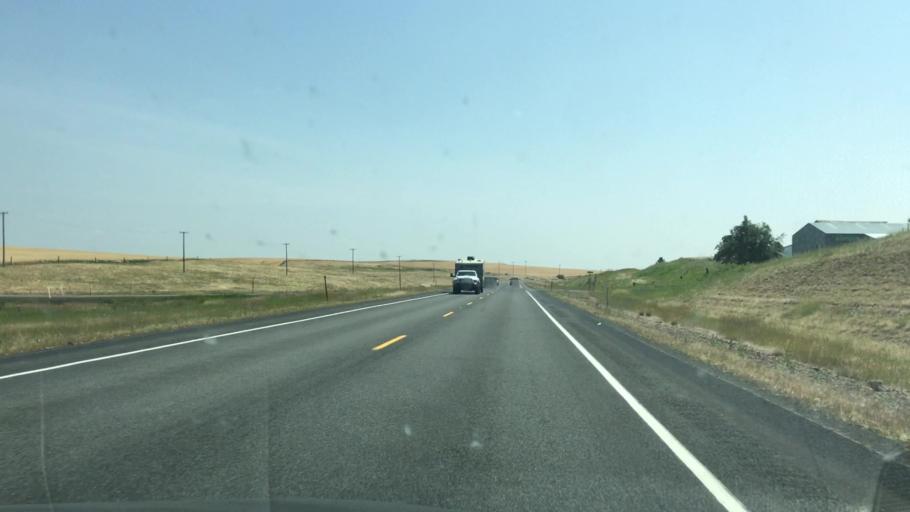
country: US
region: Idaho
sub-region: Lewis County
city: Nezperce
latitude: 46.2300
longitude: -116.4541
